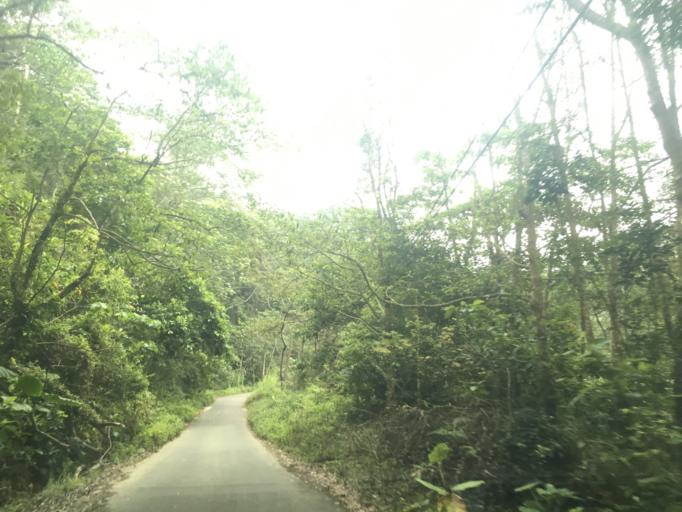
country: TW
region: Taiwan
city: Zhongxing New Village
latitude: 24.0467
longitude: 120.7869
